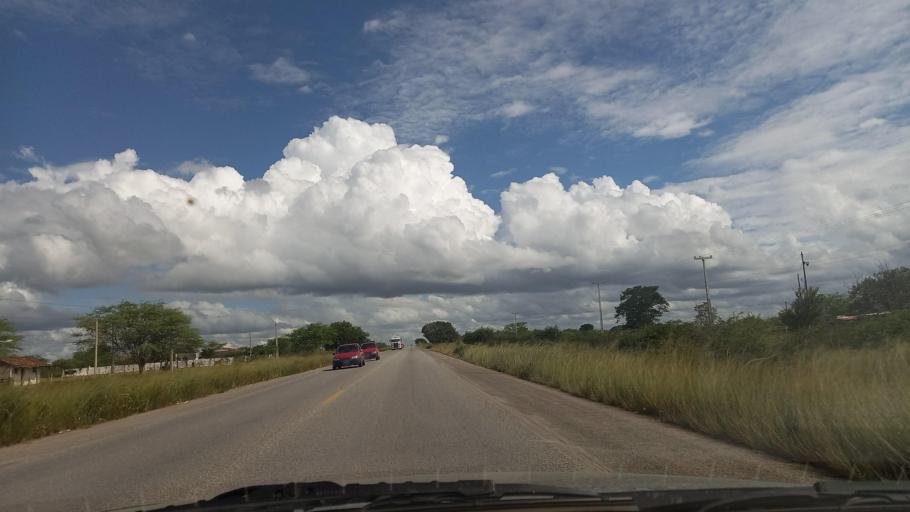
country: BR
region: Pernambuco
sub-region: Cachoeirinha
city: Cachoeirinha
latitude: -8.4606
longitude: -36.2155
